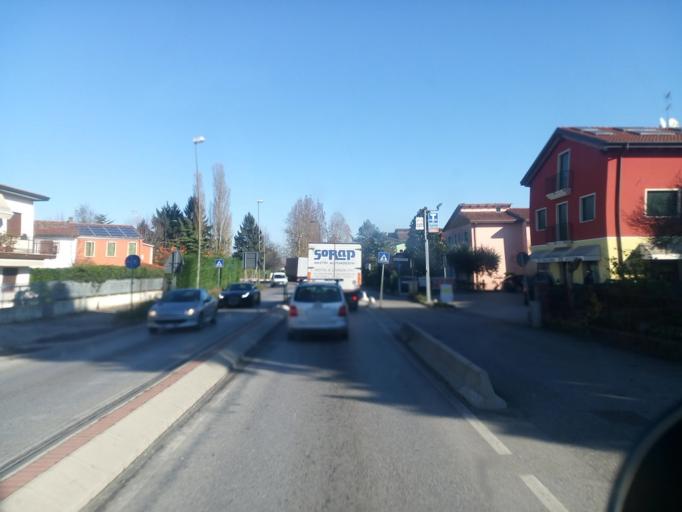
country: IT
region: Veneto
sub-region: Provincia di Padova
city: Vigonza
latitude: 45.4336
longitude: 11.9632
